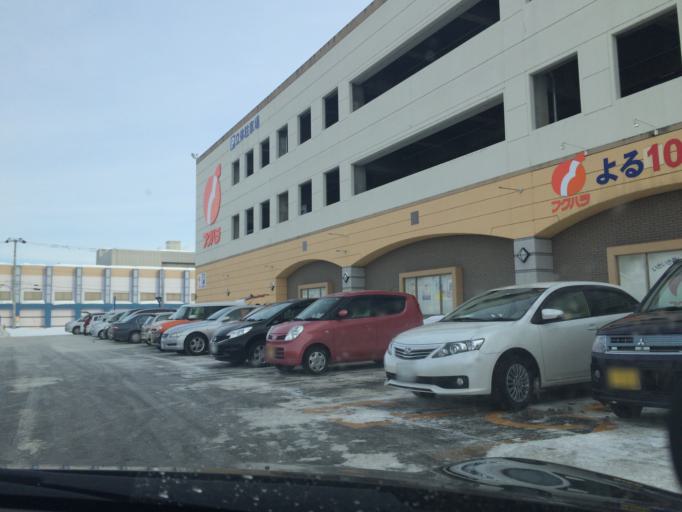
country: JP
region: Hokkaido
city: Obihiro
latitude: 42.9107
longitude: 143.0489
